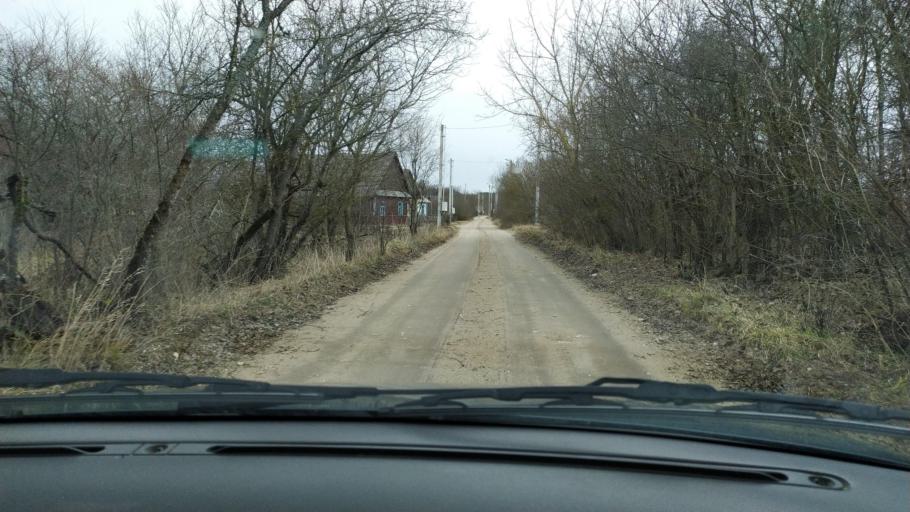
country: BY
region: Brest
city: Kamyanyets
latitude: 52.4131
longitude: 24.0245
